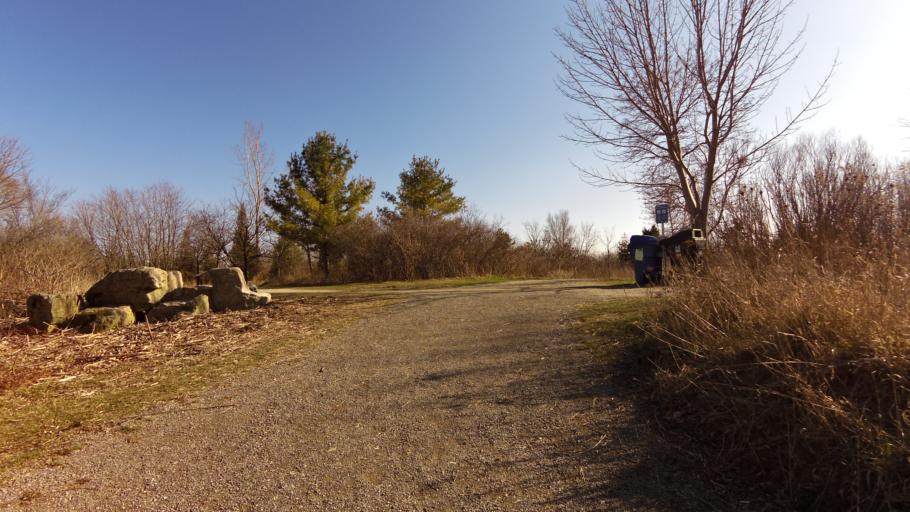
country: CA
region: Ontario
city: Etobicoke
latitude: 43.5926
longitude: -79.5122
